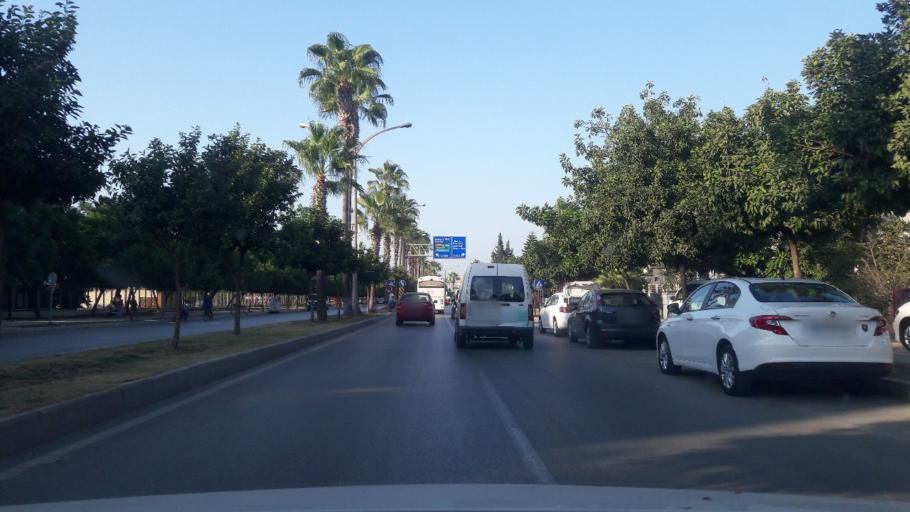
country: TR
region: Adana
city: Seyhan
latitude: 36.9904
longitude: 35.2986
